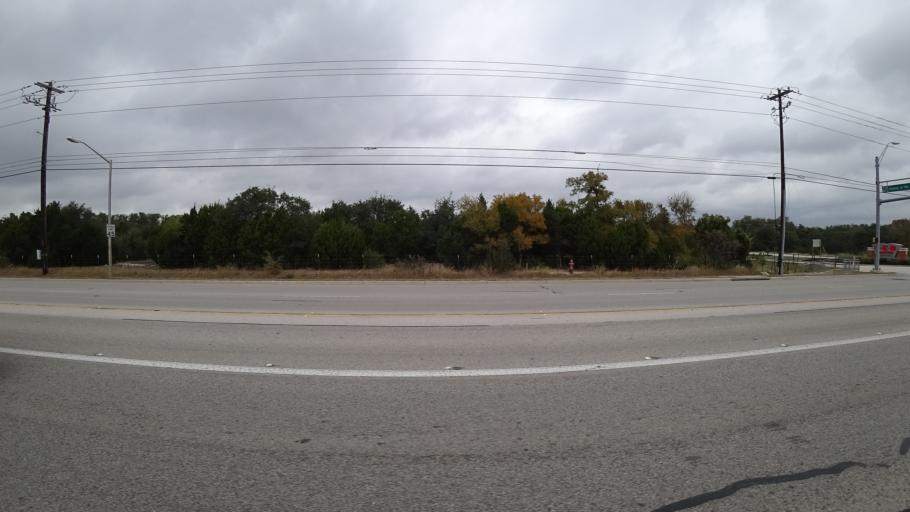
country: US
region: Texas
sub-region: Williamson County
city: Cedar Park
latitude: 30.5370
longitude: -97.8210
